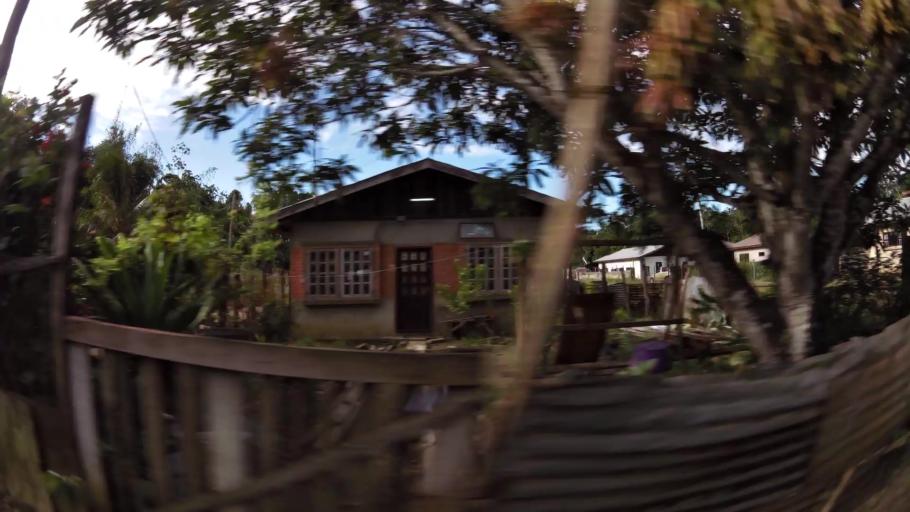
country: SR
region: Paramaribo
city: Paramaribo
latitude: 5.8454
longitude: -55.1754
